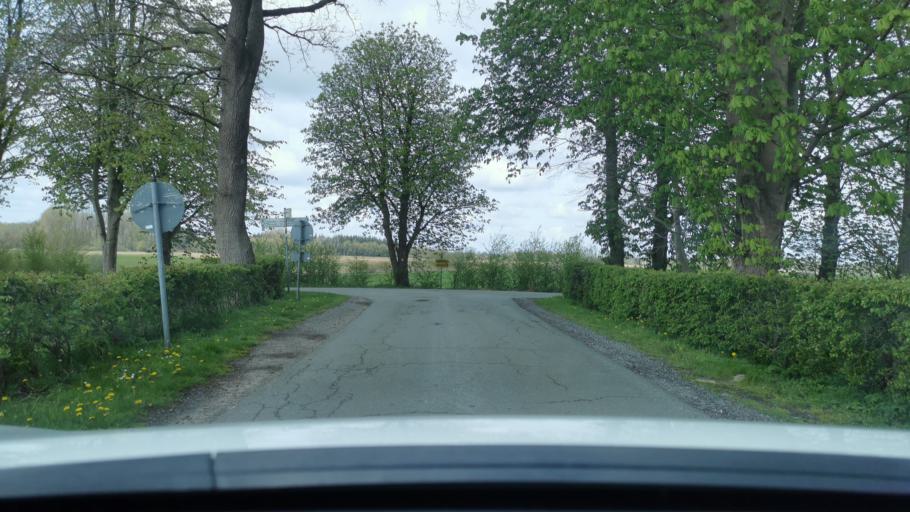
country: DE
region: Schleswig-Holstein
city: Oldenbuttel
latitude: 54.1838
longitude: 9.4408
